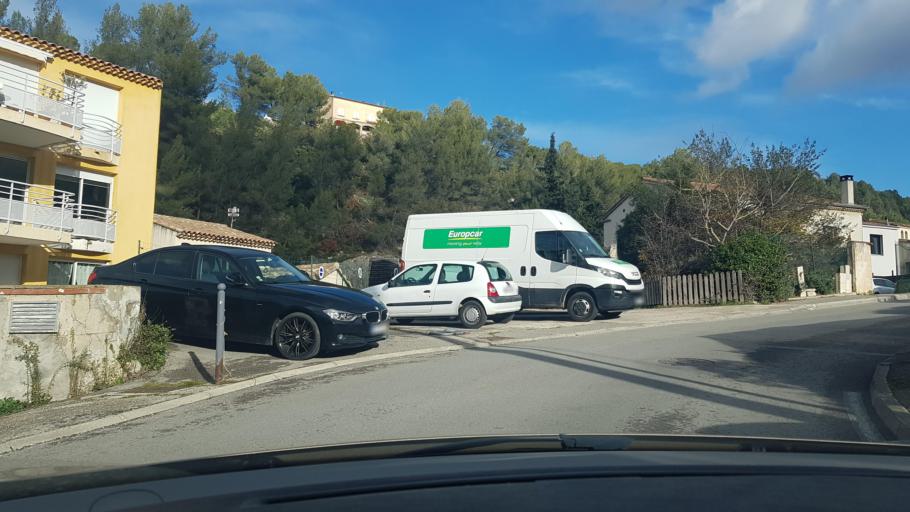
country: FR
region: Provence-Alpes-Cote d'Azur
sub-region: Departement des Bouches-du-Rhone
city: Simiane-Collongue
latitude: 43.4274
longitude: 5.4390
